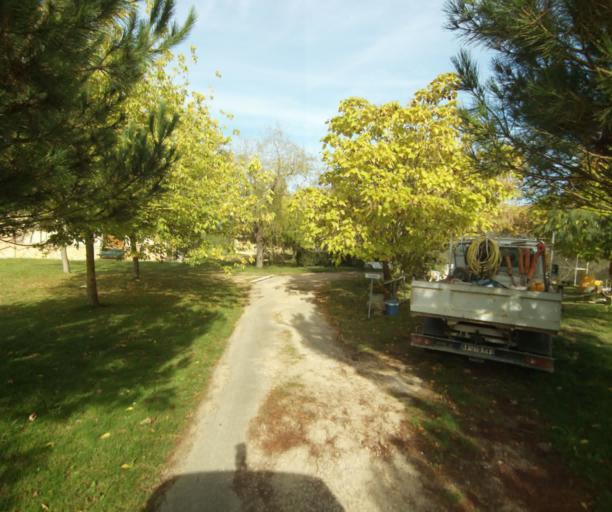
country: FR
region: Midi-Pyrenees
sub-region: Departement du Gers
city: Eauze
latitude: 43.9317
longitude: 0.0857
